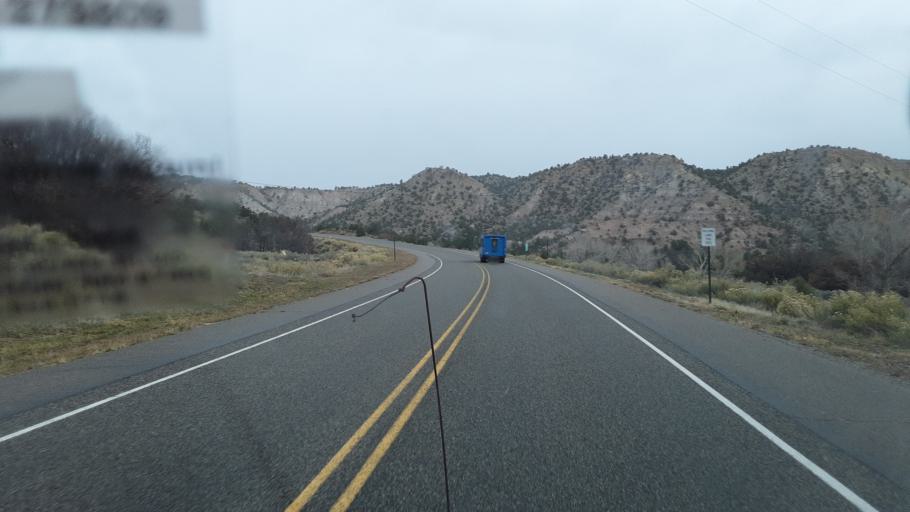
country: US
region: New Mexico
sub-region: Rio Arriba County
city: Santa Teresa
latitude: 36.3896
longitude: -106.4913
